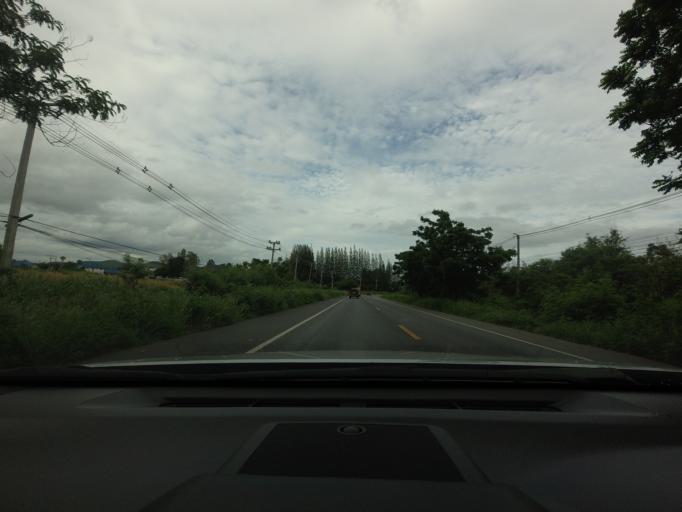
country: TH
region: Prachuap Khiri Khan
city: Hua Hin
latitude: 12.5823
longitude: 99.8554
